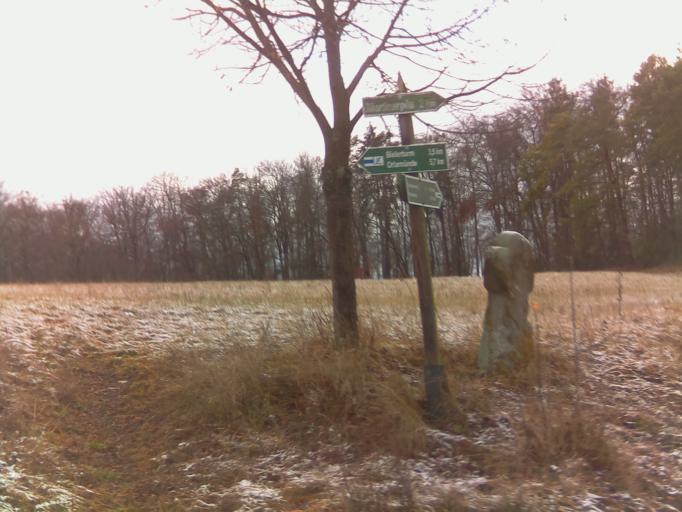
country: DE
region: Thuringia
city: Reinstadt
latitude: 50.7870
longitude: 11.4638
